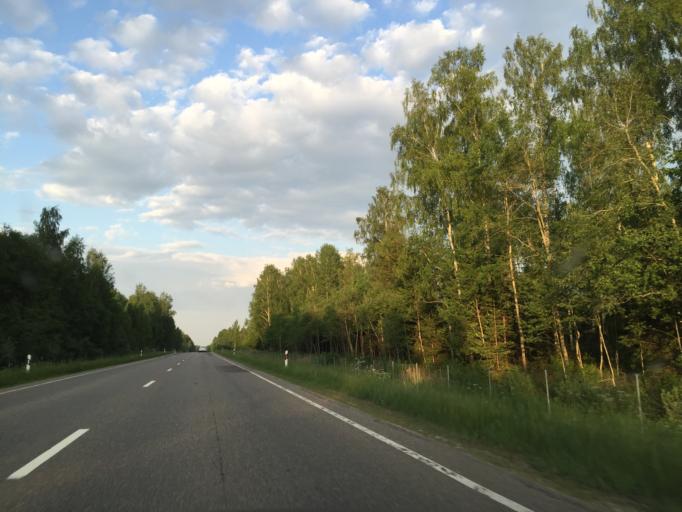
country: LT
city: Kursenai
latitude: 56.0032
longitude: 22.7617
